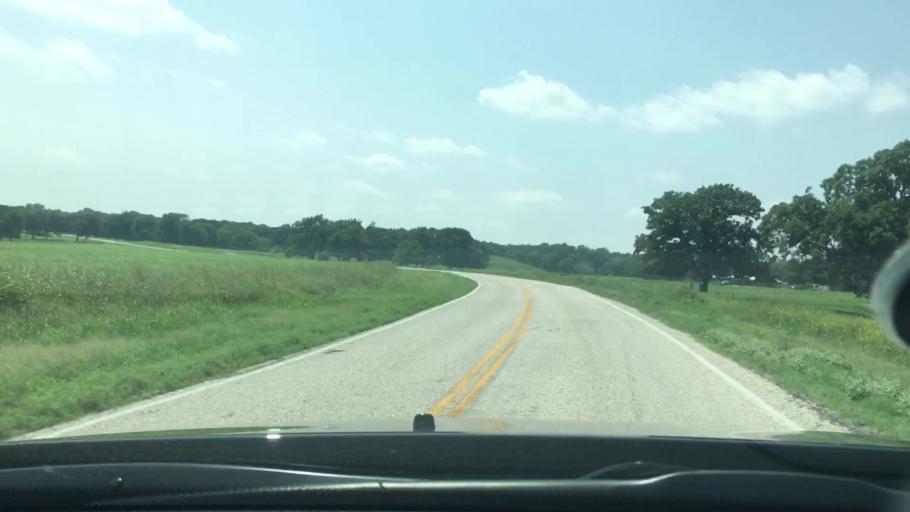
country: US
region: Oklahoma
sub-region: Johnston County
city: Tishomingo
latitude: 34.3759
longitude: -96.4916
